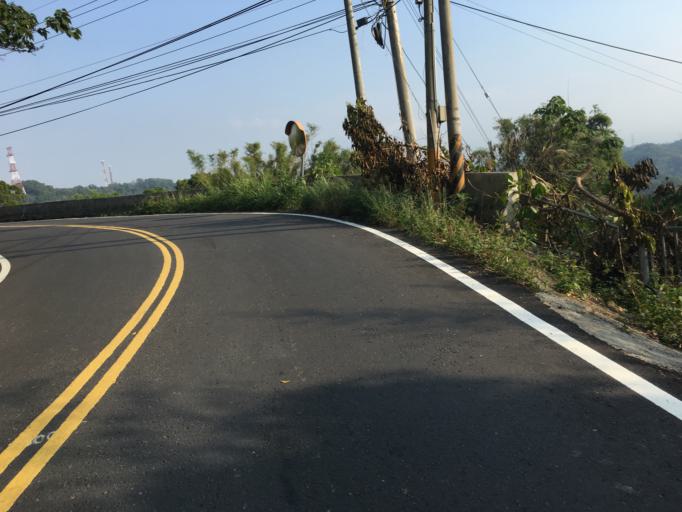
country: TW
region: Taiwan
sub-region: Hsinchu
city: Hsinchu
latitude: 24.7560
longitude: 121.0219
